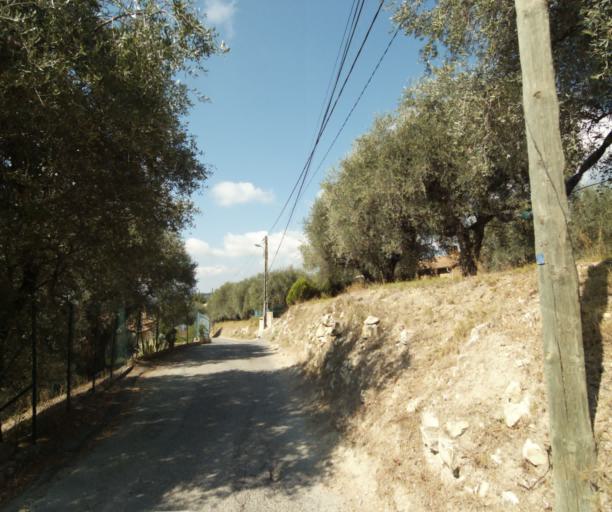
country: FR
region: Provence-Alpes-Cote d'Azur
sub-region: Departement des Alpes-Maritimes
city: Drap
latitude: 43.7481
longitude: 7.3281
